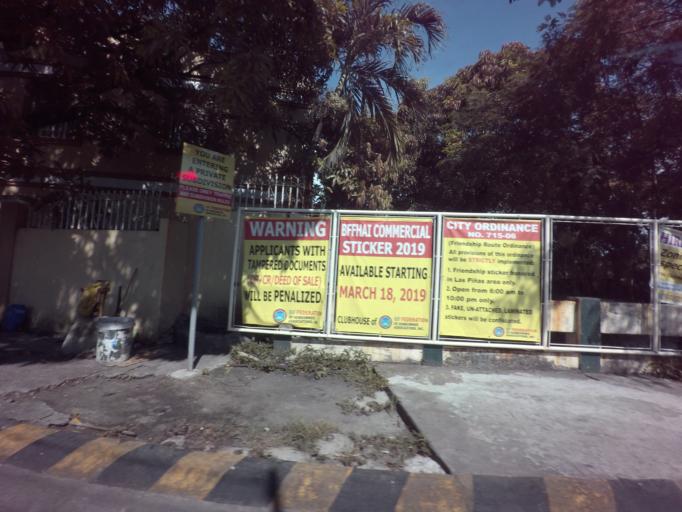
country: PH
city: Sambayanihan People's Village
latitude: 14.4433
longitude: 121.0080
